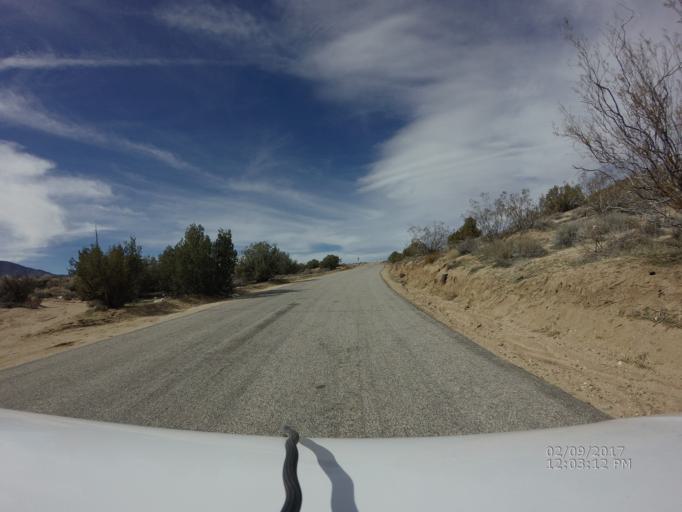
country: US
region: California
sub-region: Los Angeles County
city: Littlerock
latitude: 34.4772
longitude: -117.9040
